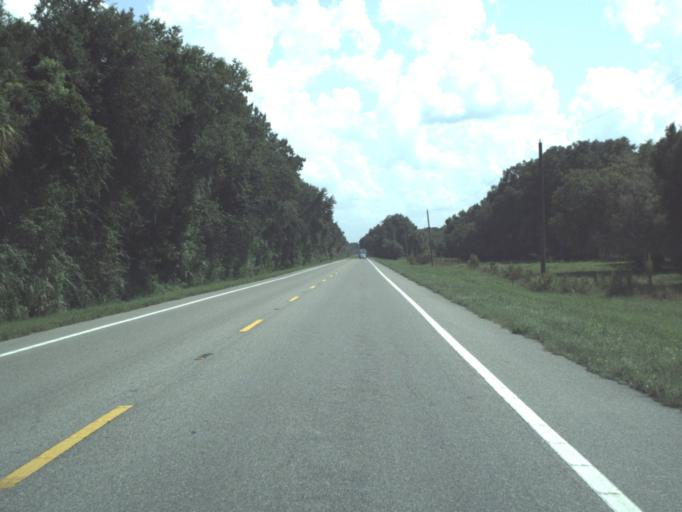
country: US
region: Florida
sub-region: Pasco County
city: Zephyrhills South
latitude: 28.1609
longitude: -82.2167
